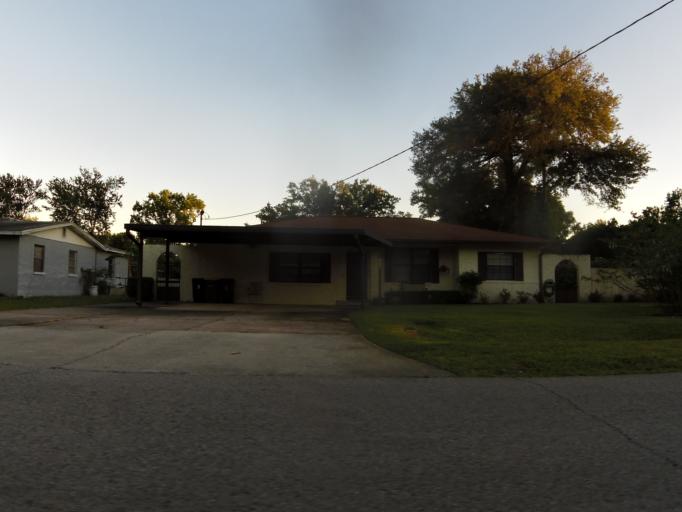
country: US
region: Florida
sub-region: Duval County
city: Jacksonville
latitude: 30.2636
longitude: -81.6346
